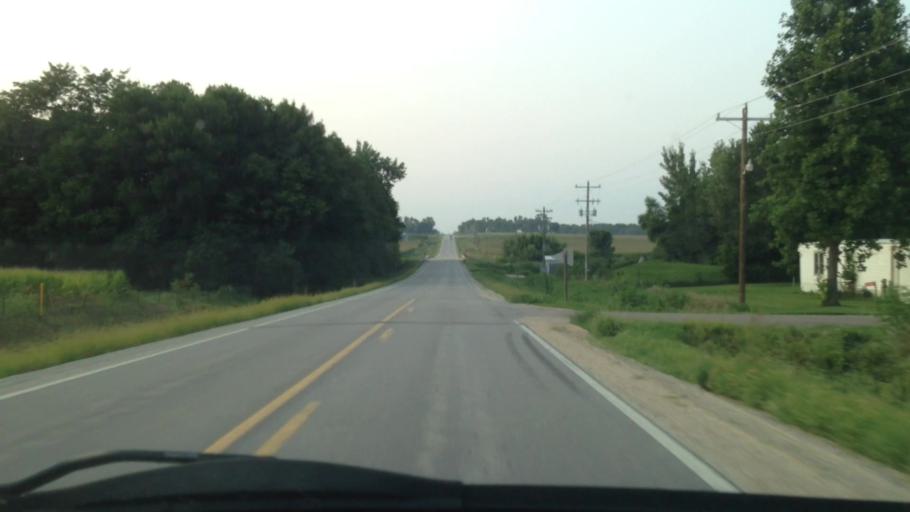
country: US
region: Iowa
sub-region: Benton County
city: Atkins
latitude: 42.0566
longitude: -91.8692
